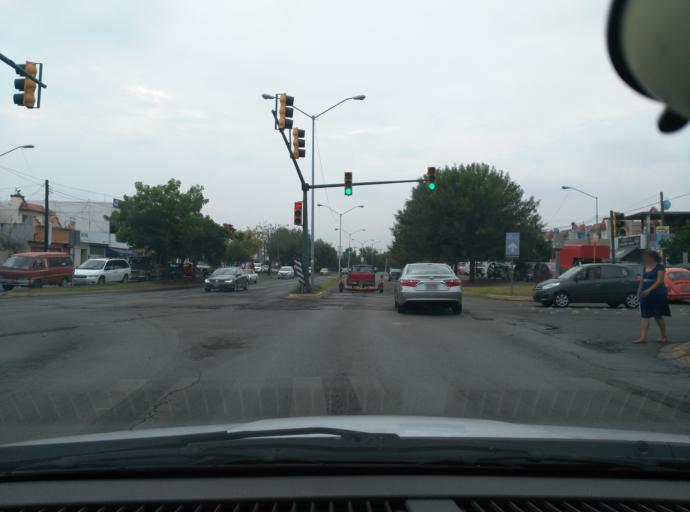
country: MX
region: Nuevo Leon
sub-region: Apodaca
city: Fraccionamiento Cosmopolis Octavo Sector
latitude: 25.7715
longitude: -100.2525
